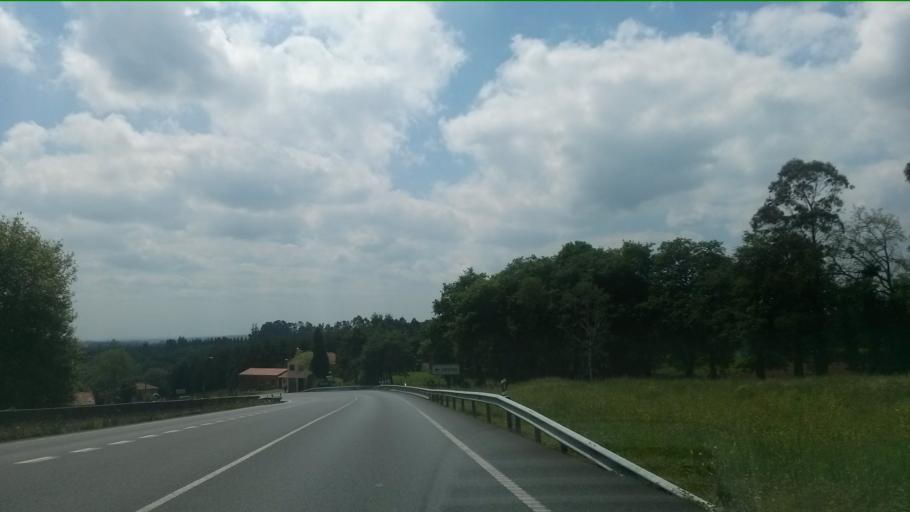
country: ES
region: Galicia
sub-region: Provincia da Coruna
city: Mesia
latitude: 43.0878
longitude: -8.1847
